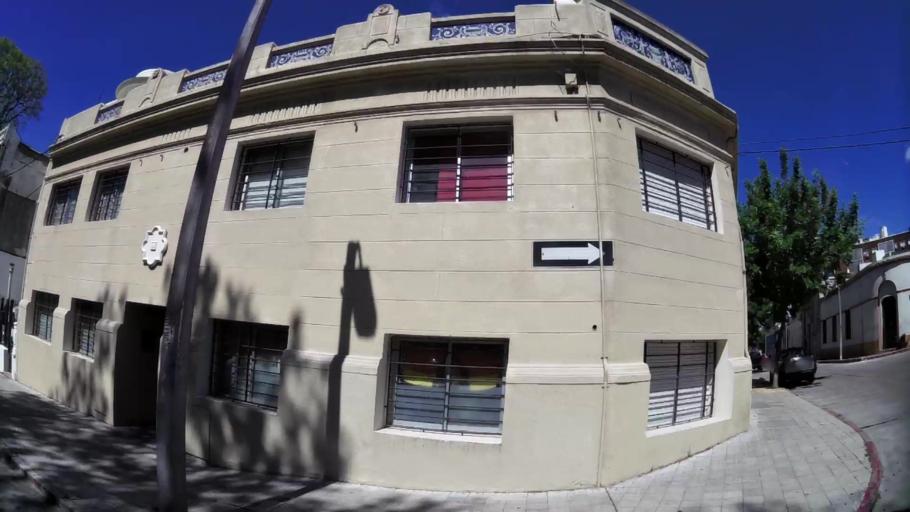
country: UY
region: Montevideo
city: Montevideo
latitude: -34.8936
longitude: -56.1864
